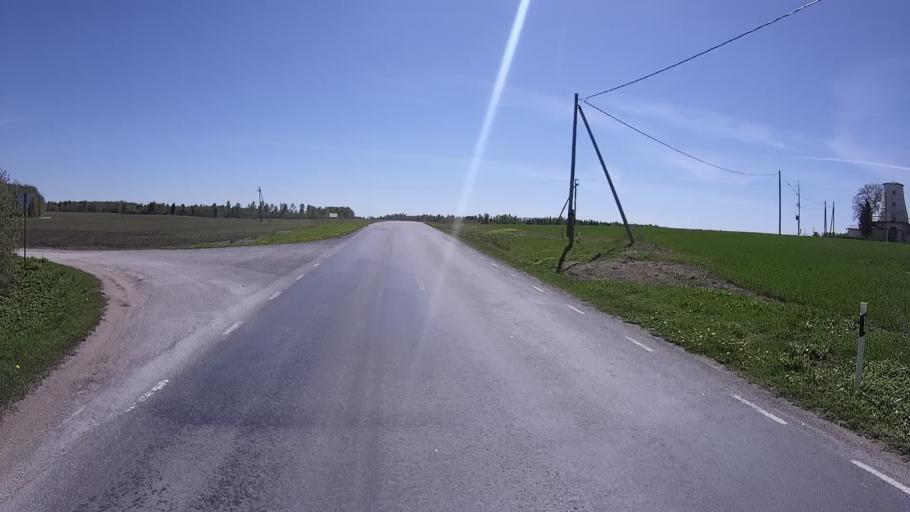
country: EE
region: Harju
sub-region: Raasiku vald
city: Raasiku
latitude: 59.1015
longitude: 25.1695
